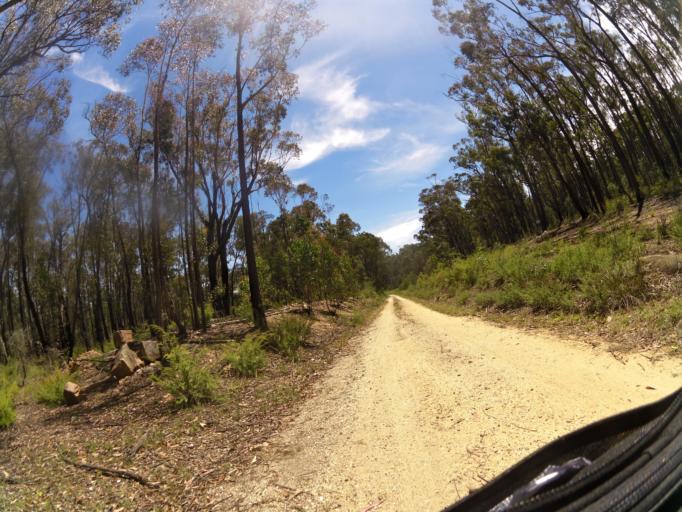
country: AU
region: Victoria
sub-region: East Gippsland
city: Lakes Entrance
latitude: -37.7589
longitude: 147.9313
